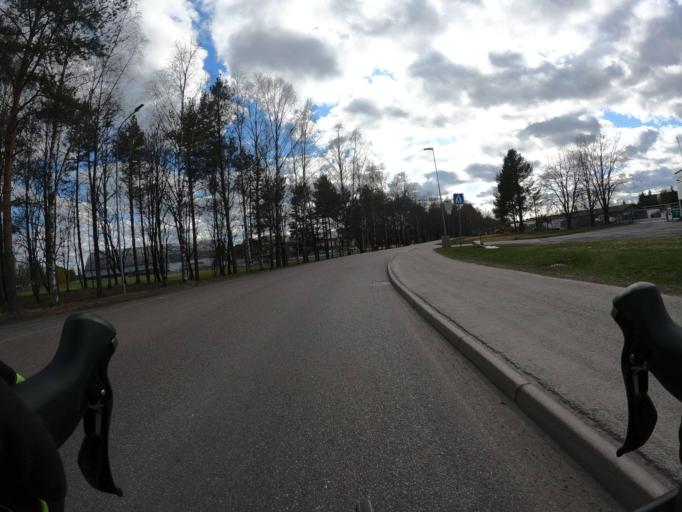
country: NO
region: Akershus
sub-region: Skedsmo
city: Lillestrom
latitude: 59.9639
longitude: 11.0706
